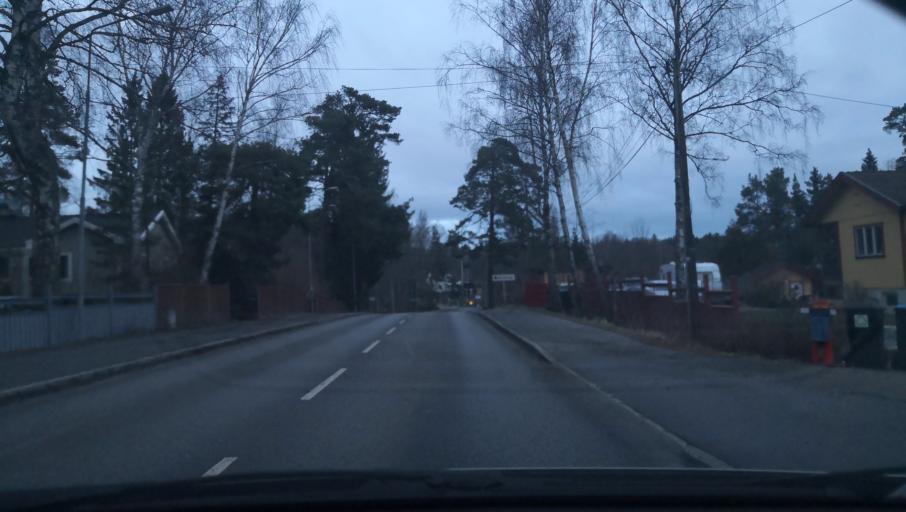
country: SE
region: Stockholm
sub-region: Taby Kommun
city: Taby
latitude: 59.4511
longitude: 18.0696
